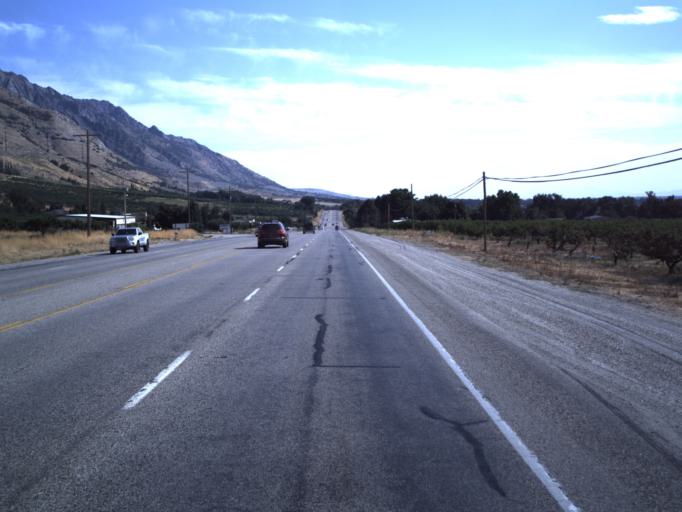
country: US
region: Utah
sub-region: Box Elder County
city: Perry
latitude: 41.4514
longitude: -112.0384
